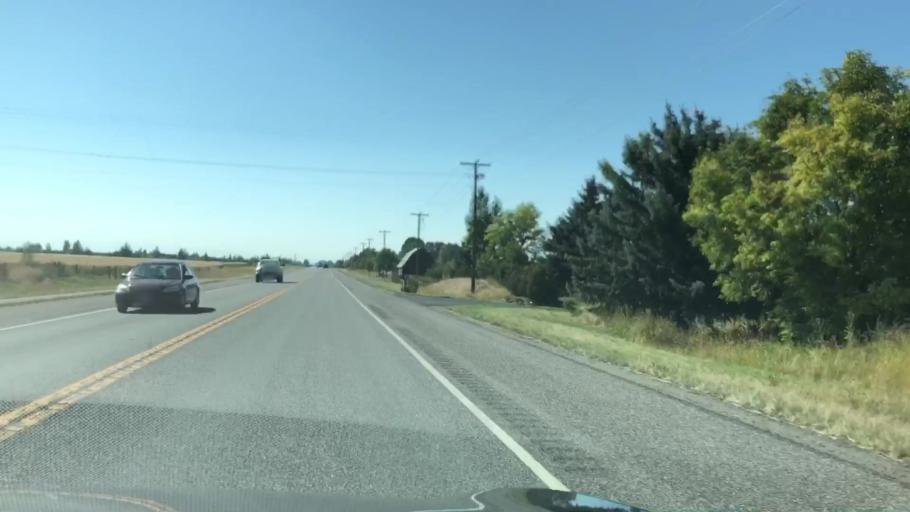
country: US
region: Montana
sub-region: Gallatin County
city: Belgrade
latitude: 45.7292
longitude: -111.1134
